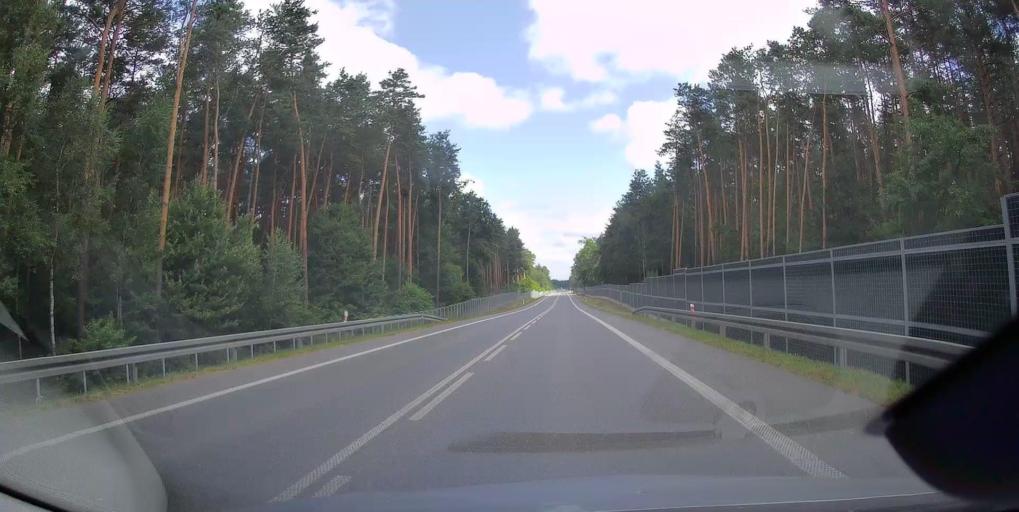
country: PL
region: Subcarpathian Voivodeship
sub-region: Powiat mielecki
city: Mielec
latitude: 50.2988
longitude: 21.4945
